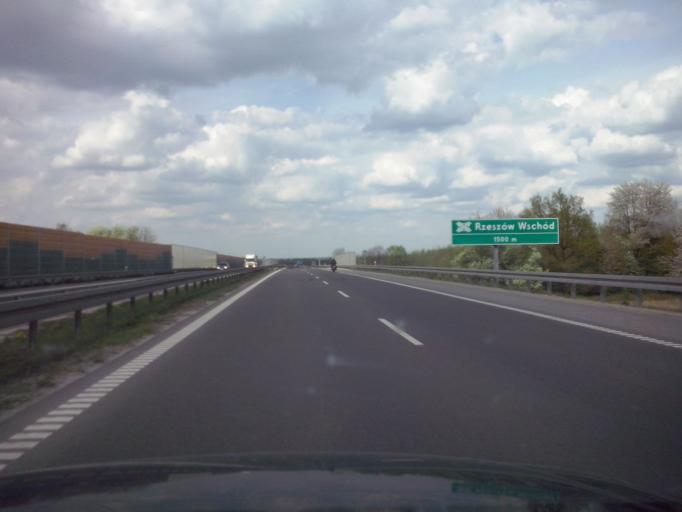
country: PL
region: Subcarpathian Voivodeship
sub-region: Powiat rzeszowski
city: Trzebownisko
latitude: 50.0750
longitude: 22.0584
